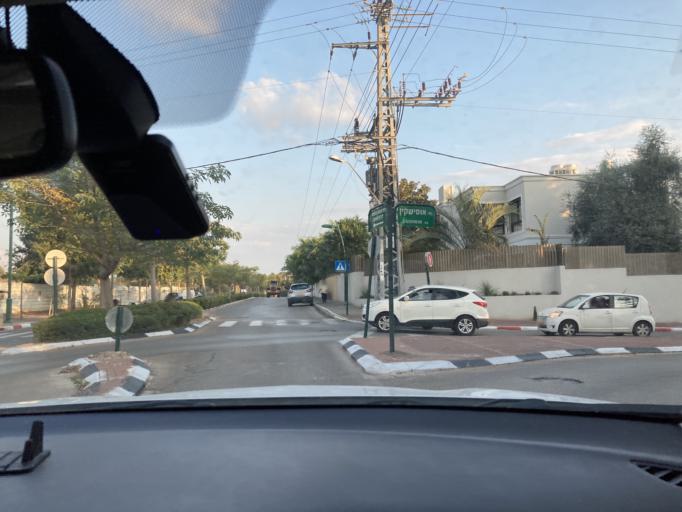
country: IL
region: Tel Aviv
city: Ramat HaSharon
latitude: 32.1498
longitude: 34.8464
